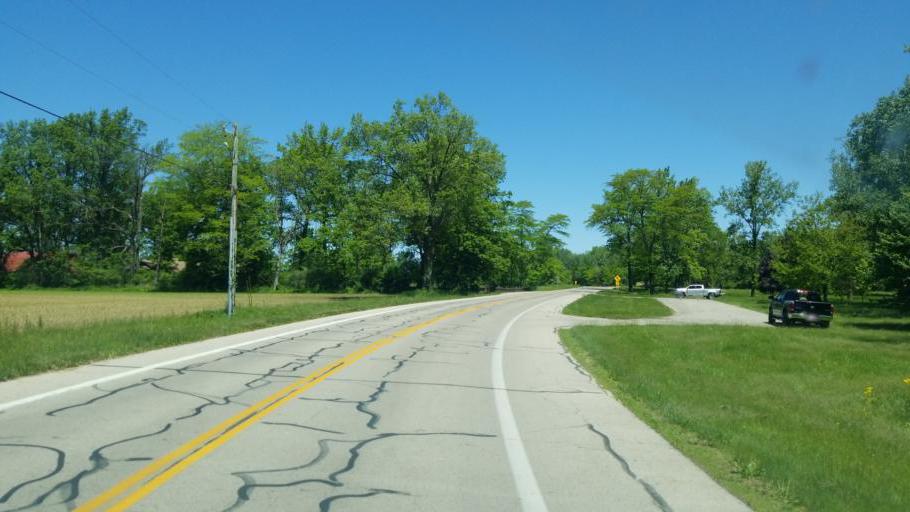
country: US
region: Ohio
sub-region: Auglaize County
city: Minster
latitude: 40.3808
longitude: -84.3597
